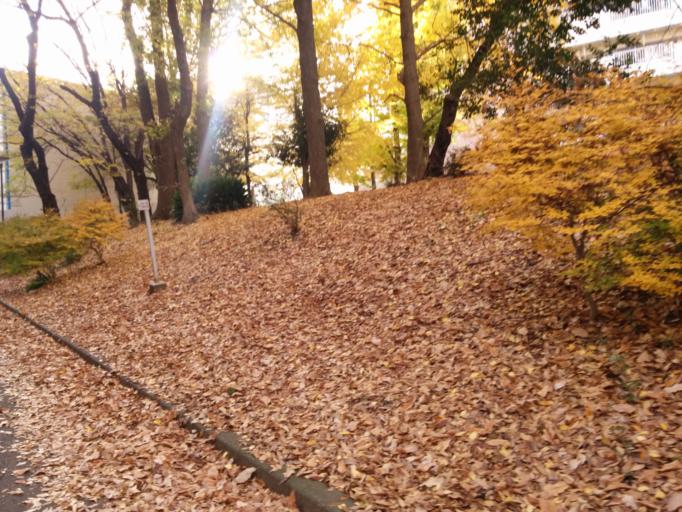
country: JP
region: Tokyo
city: Tokyo
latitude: 35.7014
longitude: 139.7099
